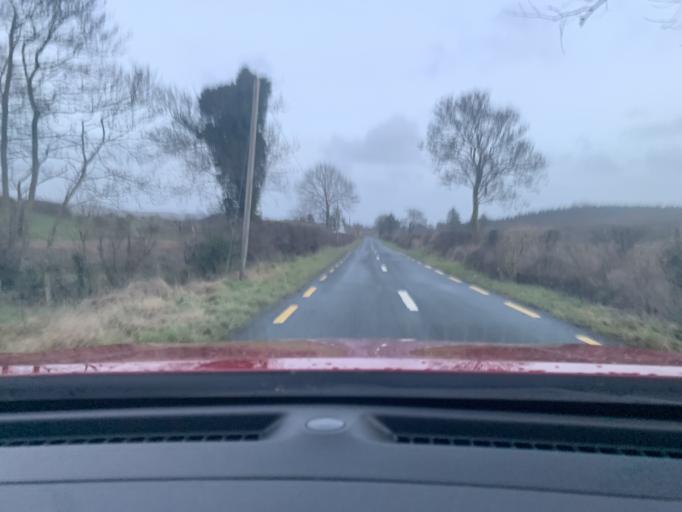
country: IE
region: Connaught
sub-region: Sligo
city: Ballymote
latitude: 54.0413
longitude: -8.4373
